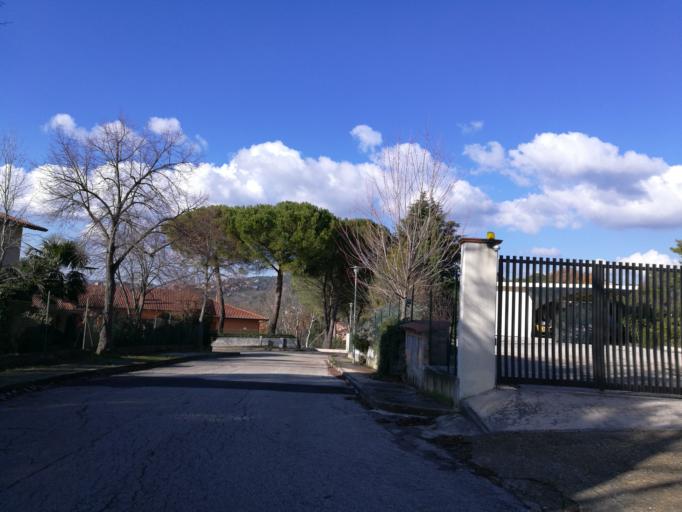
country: IT
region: Umbria
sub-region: Provincia di Perugia
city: Perugia
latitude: 43.0814
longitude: 12.3754
